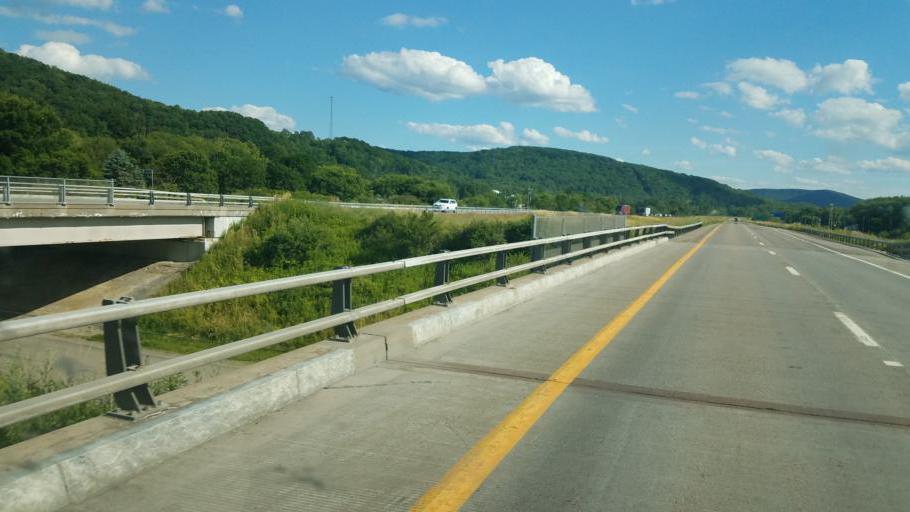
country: US
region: New York
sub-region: Cattaraugus County
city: Olean
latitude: 42.1204
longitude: -78.4180
